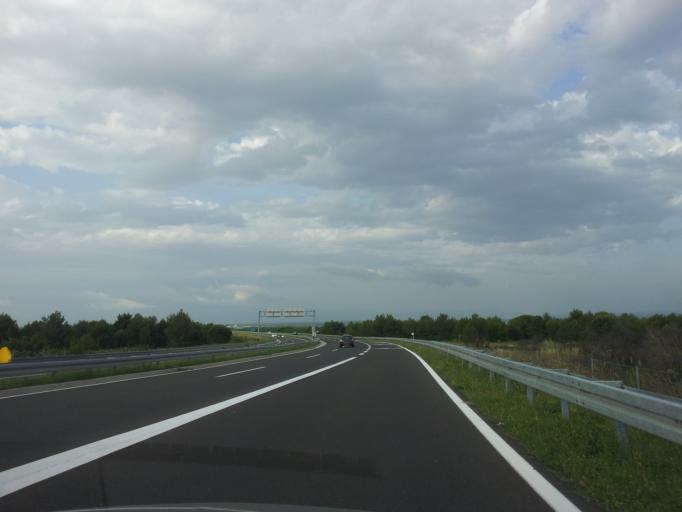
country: HR
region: Zadarska
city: Sukosan
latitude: 44.0717
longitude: 15.3420
